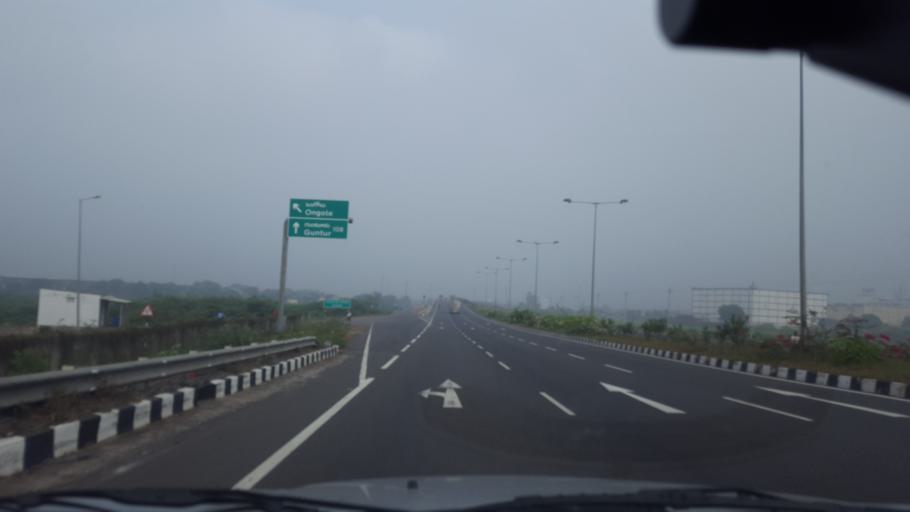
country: IN
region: Andhra Pradesh
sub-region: Prakasam
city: Ongole
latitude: 15.5290
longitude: 80.0560
